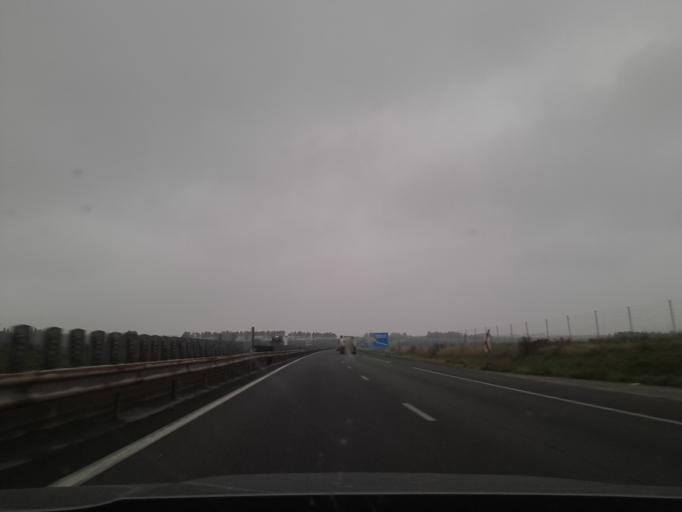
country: FR
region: Nord-Pas-de-Calais
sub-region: Departement du Nord
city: Fontaine-Notre-Dame
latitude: 50.1663
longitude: 3.1750
